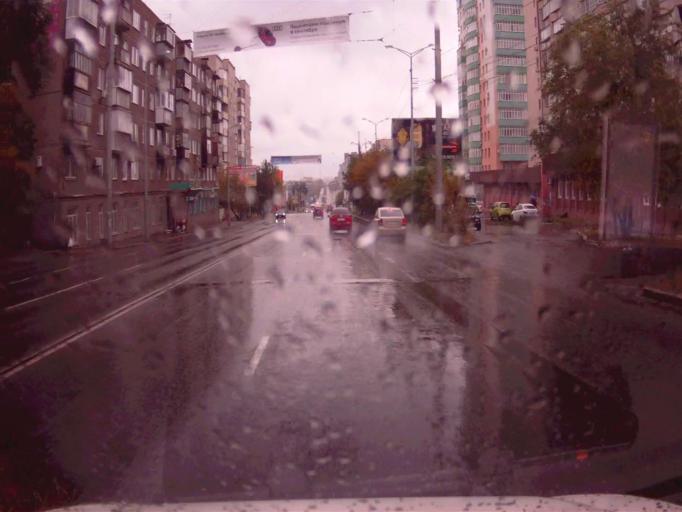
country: RU
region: Chelyabinsk
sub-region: Gorod Chelyabinsk
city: Chelyabinsk
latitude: 55.1614
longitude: 61.4164
